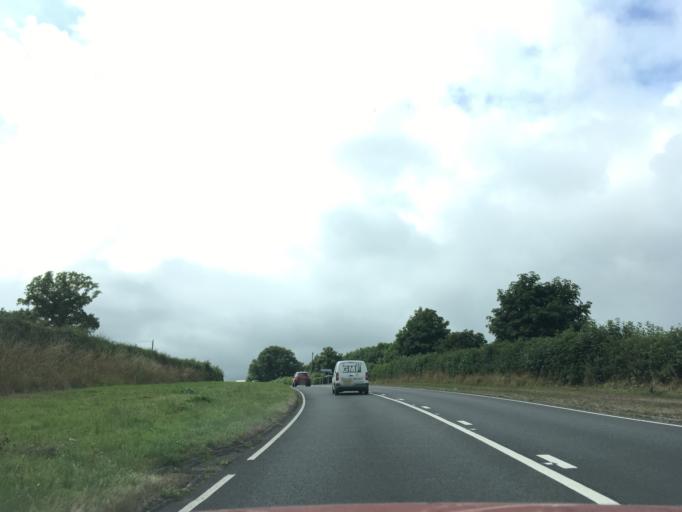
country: GB
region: Wales
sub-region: Carmarthenshire
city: Llanddarog
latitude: 51.8739
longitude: -4.1520
